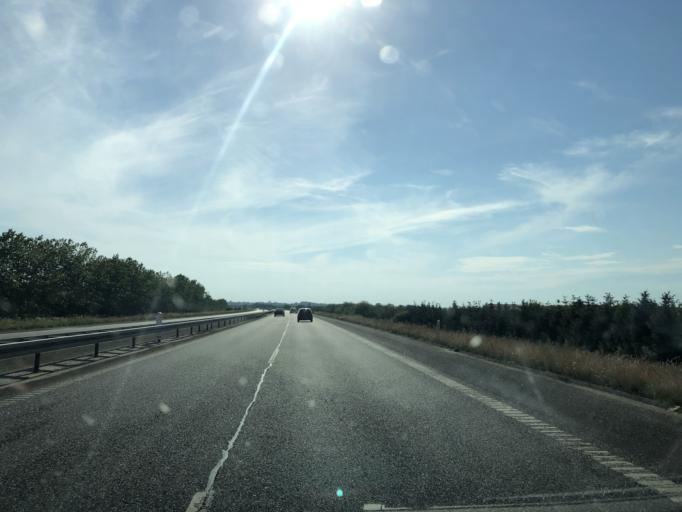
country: DK
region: Central Jutland
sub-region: Ikast-Brande Kommune
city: Bording Kirkeby
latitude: 56.1342
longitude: 9.2444
